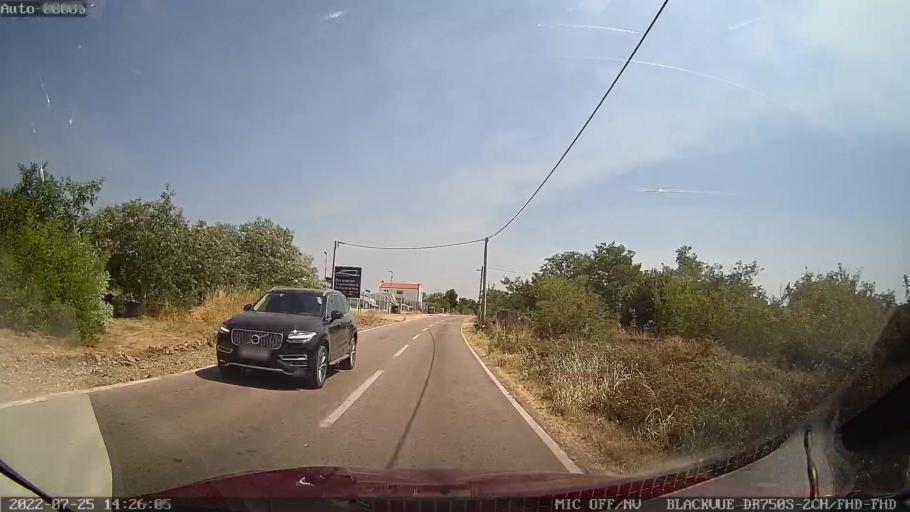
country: HR
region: Zadarska
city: Policnik
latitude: 44.1410
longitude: 15.3359
